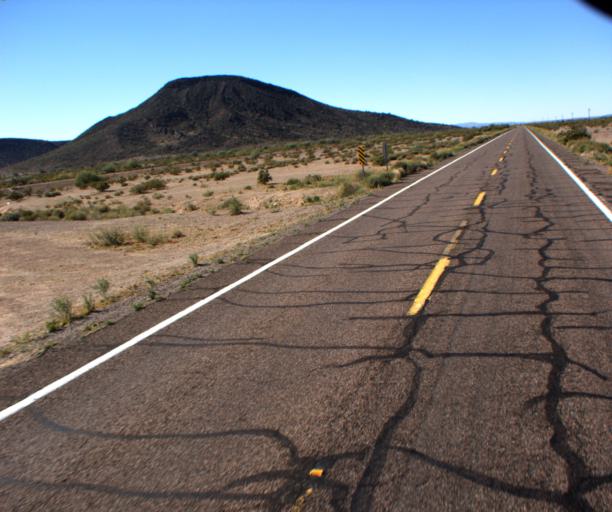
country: US
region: Arizona
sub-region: Maricopa County
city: Gila Bend
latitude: 32.7664
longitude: -112.8183
